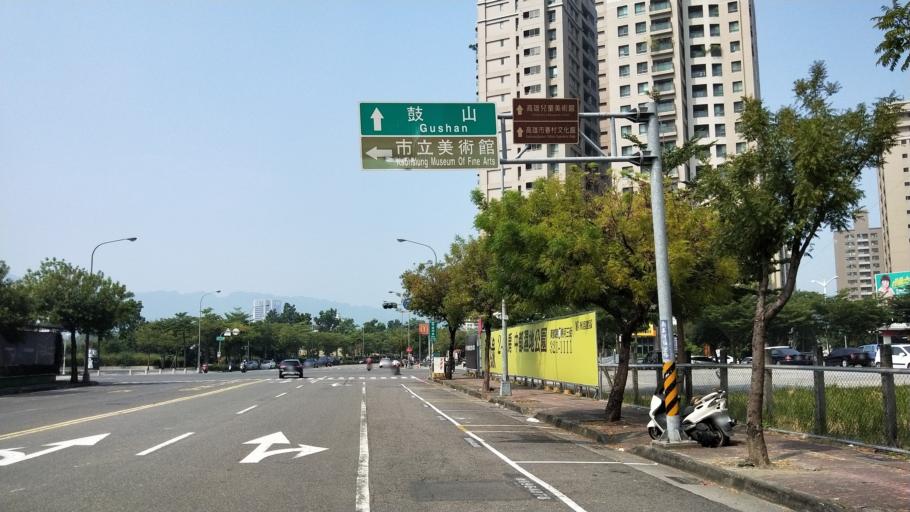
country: TW
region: Kaohsiung
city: Kaohsiung
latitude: 22.6613
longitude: 120.2892
